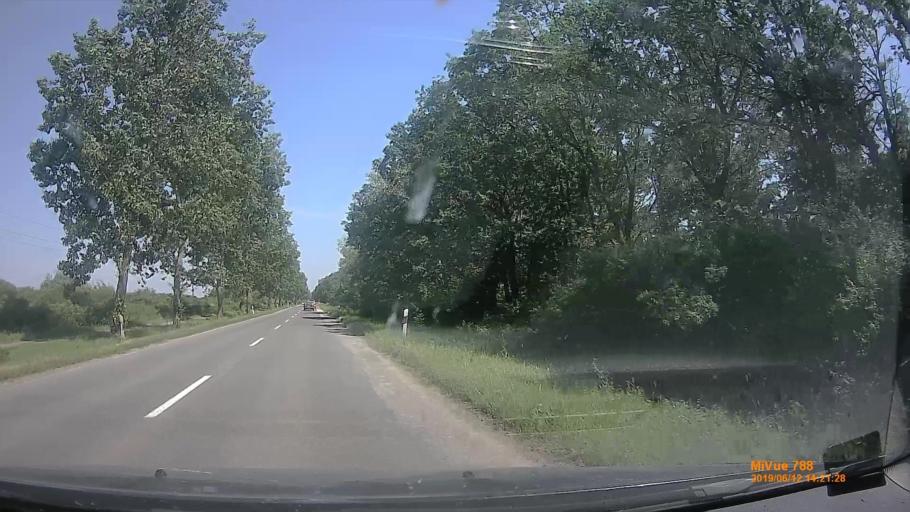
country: HU
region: Csongrad
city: Deszk
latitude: 46.2196
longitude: 20.2590
